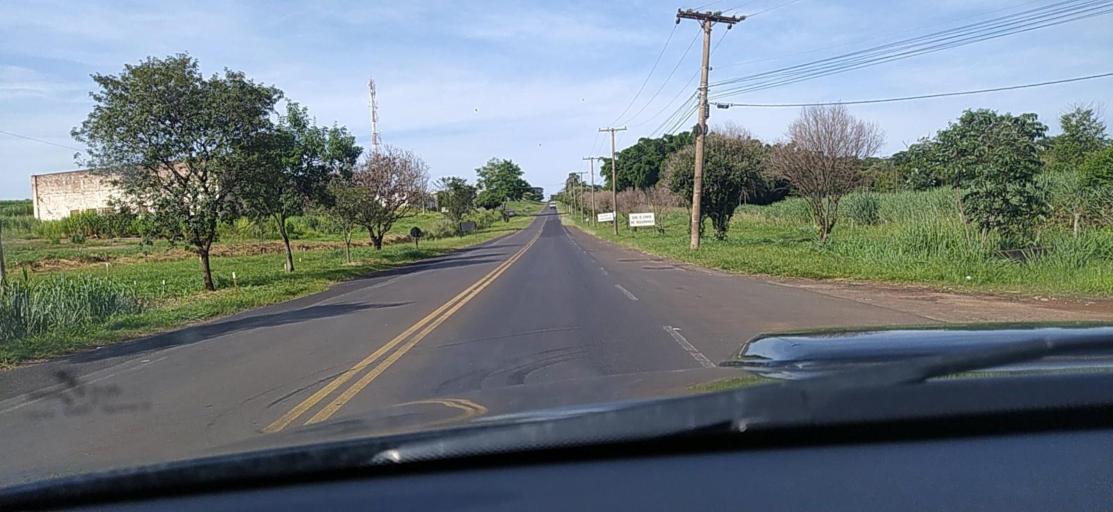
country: BR
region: Sao Paulo
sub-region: Pindorama
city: Pindorama
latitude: -21.1931
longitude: -48.9149
